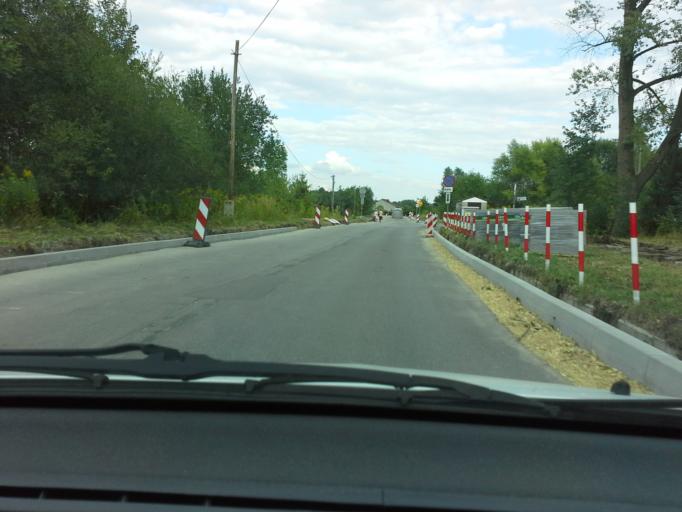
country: PL
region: Lesser Poland Voivodeship
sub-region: Powiat chrzanowski
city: Chrzanow
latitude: 50.1383
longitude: 19.4312
